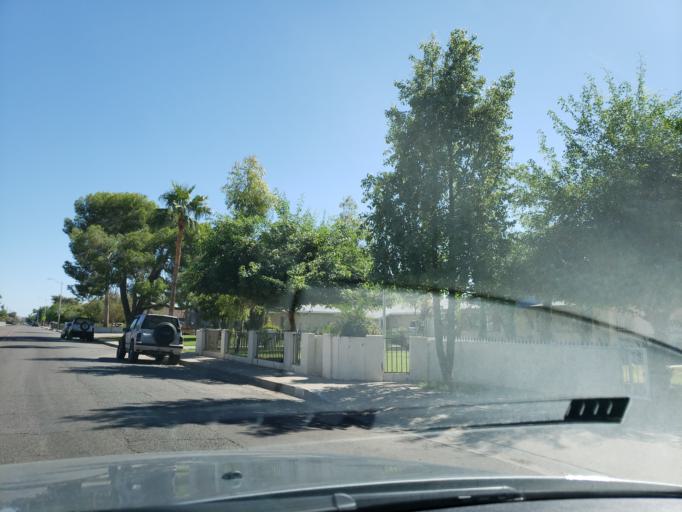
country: US
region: Arizona
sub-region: Maricopa County
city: Glendale
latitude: 33.5021
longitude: -112.2000
